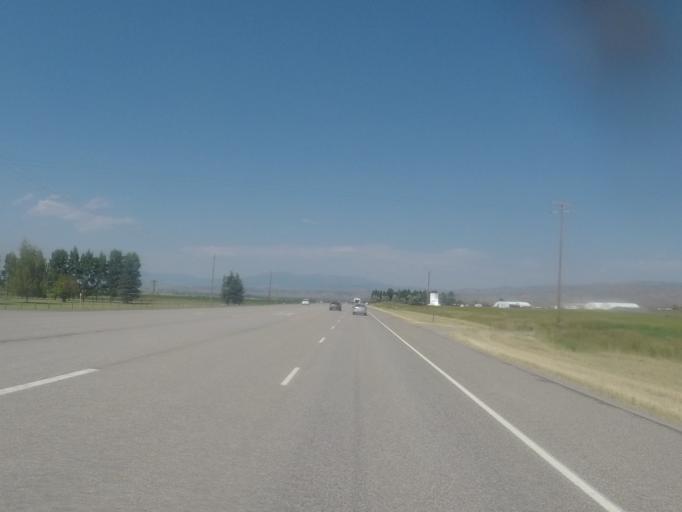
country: US
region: Montana
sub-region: Broadwater County
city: Townsend
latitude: 46.1358
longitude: -111.4820
